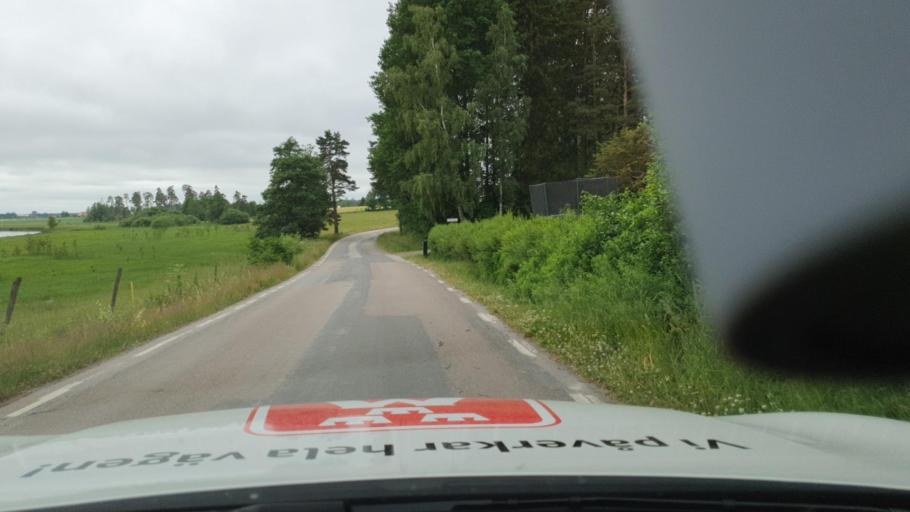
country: SE
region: Vaestra Goetaland
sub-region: Tibro Kommun
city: Tibro
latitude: 58.3984
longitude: 14.1226
